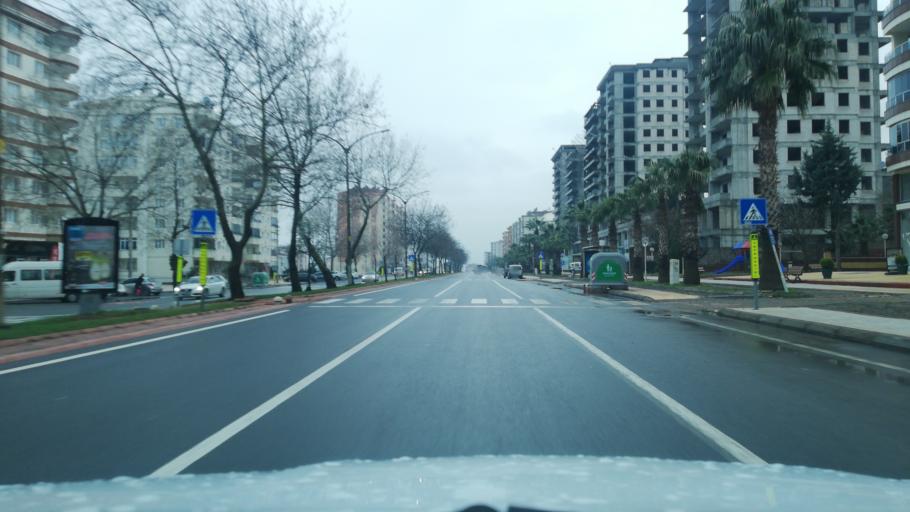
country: TR
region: Kahramanmaras
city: Kahramanmaras
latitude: 37.5919
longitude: 36.8672
